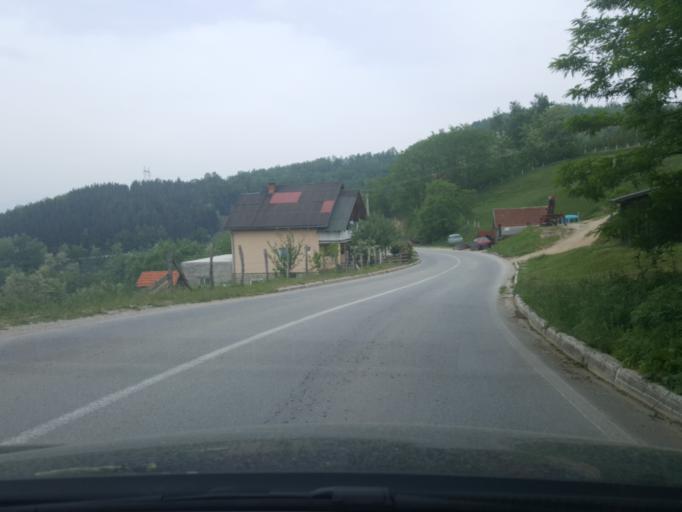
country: RS
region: Central Serbia
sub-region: Zlatiborski Okrug
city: Bajina Basta
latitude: 43.9281
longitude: 19.5684
